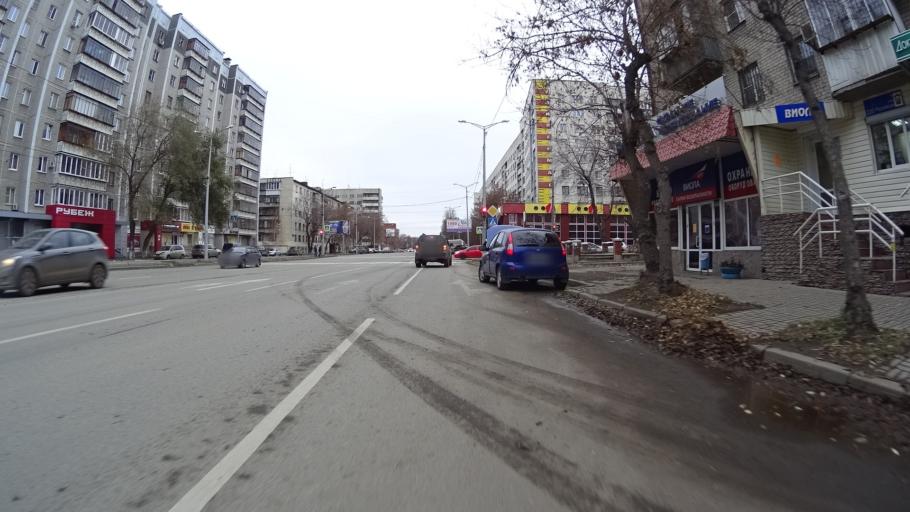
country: RU
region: Chelyabinsk
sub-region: Gorod Chelyabinsk
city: Chelyabinsk
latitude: 55.1565
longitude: 61.4175
